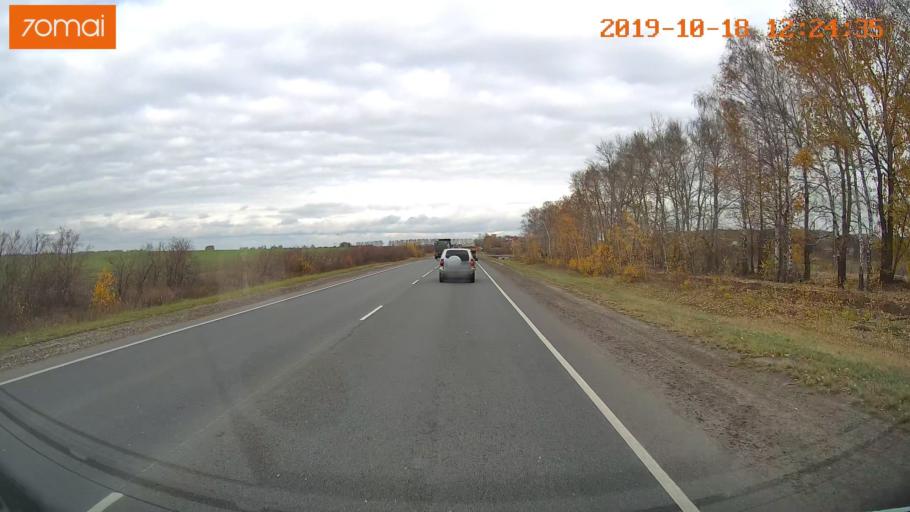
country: RU
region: Rjazan
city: Rybnoye
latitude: 54.5405
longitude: 39.5141
